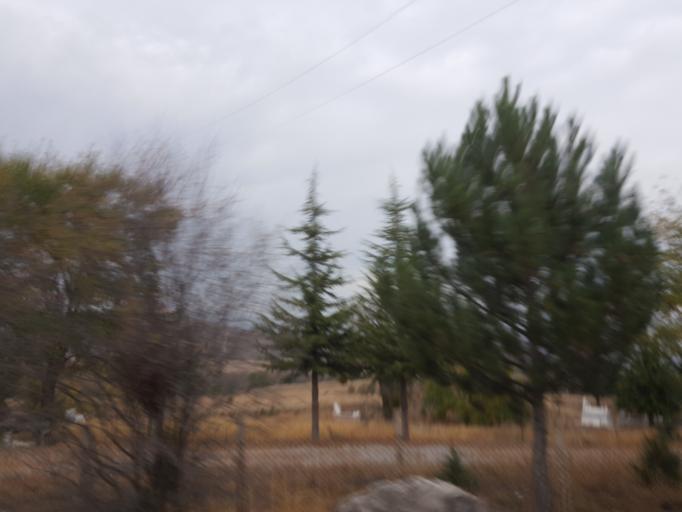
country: TR
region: Corum
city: Cemilbey
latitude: 40.2822
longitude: 35.0604
